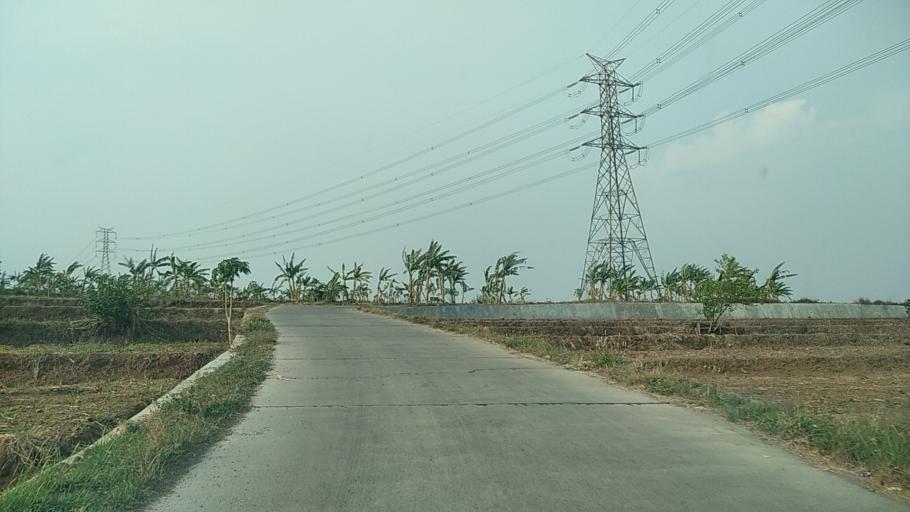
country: ID
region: Central Java
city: Mranggen
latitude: -7.0663
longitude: 110.4934
